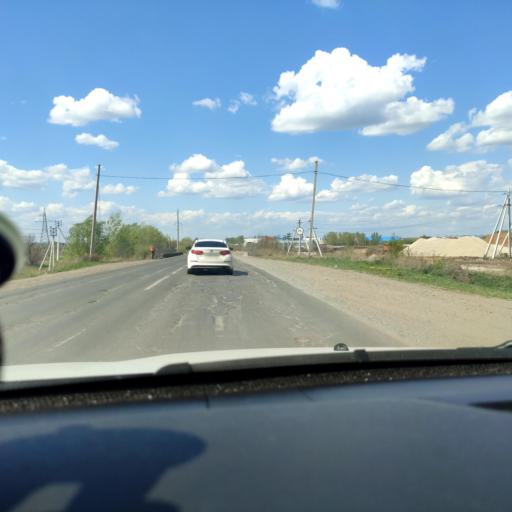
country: RU
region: Samara
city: Kinel'
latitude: 53.2207
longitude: 50.6043
